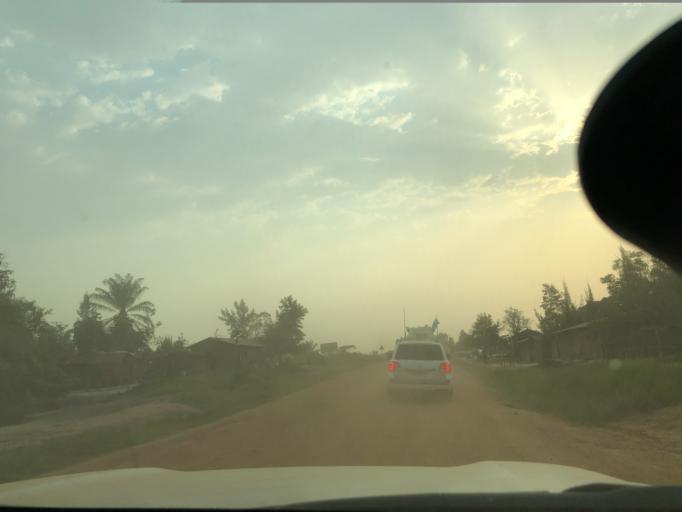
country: CD
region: Nord Kivu
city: Beni
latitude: 0.3501
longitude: 29.6512
